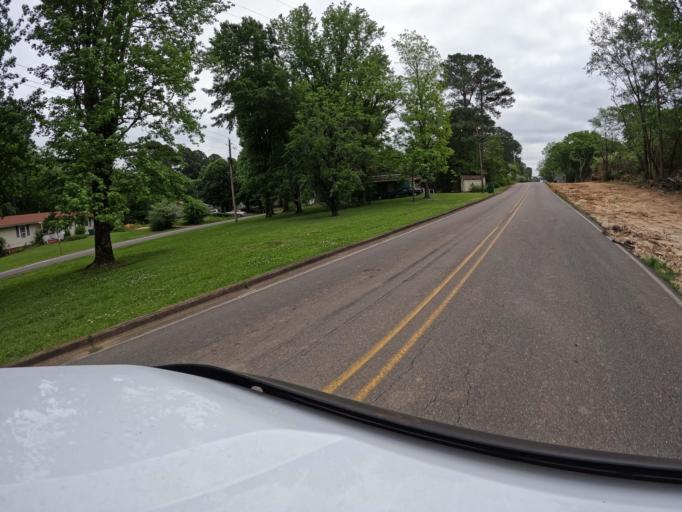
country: US
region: Mississippi
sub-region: Lee County
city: Tupelo
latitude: 34.2776
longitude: -88.7333
